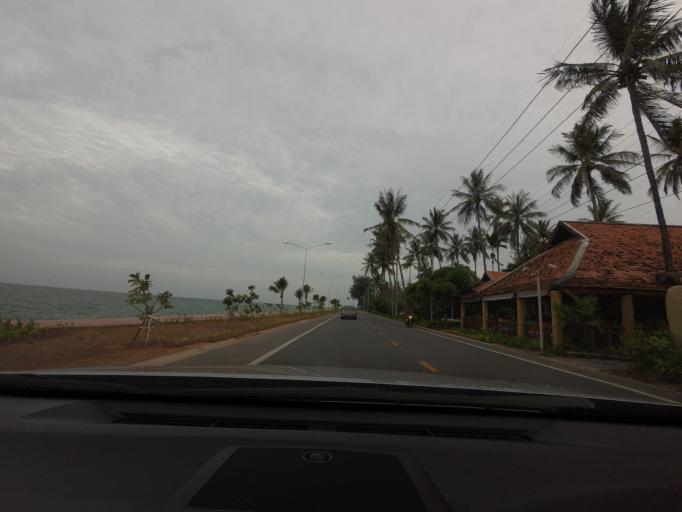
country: TH
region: Prachuap Khiri Khan
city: Pran Buri
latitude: 12.3859
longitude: 99.9989
